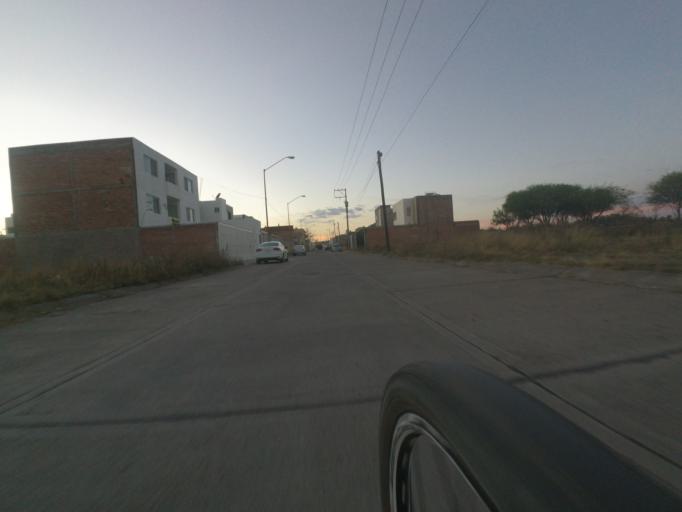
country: MX
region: Aguascalientes
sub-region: Aguascalientes
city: La Loma de los Negritos
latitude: 21.8504
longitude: -102.3299
